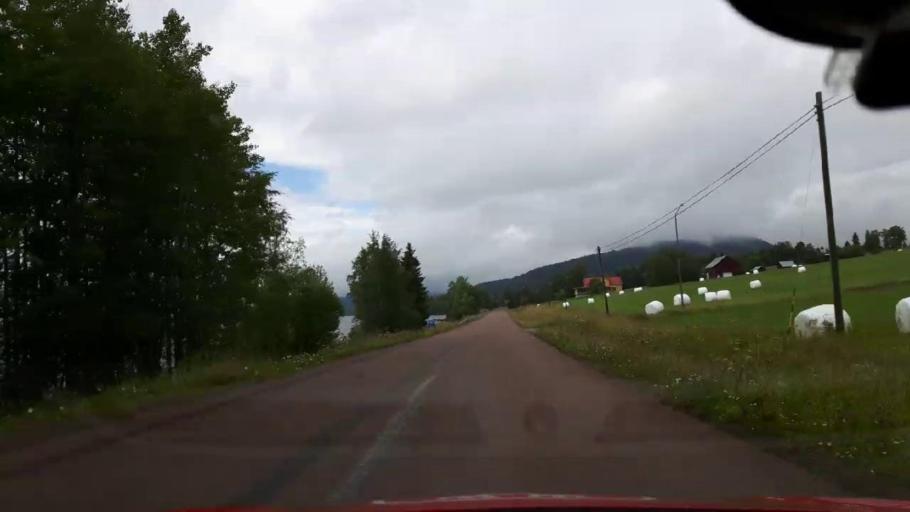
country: SE
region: Jaemtland
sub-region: Krokoms Kommun
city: Valla
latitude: 63.3711
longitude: 14.0339
